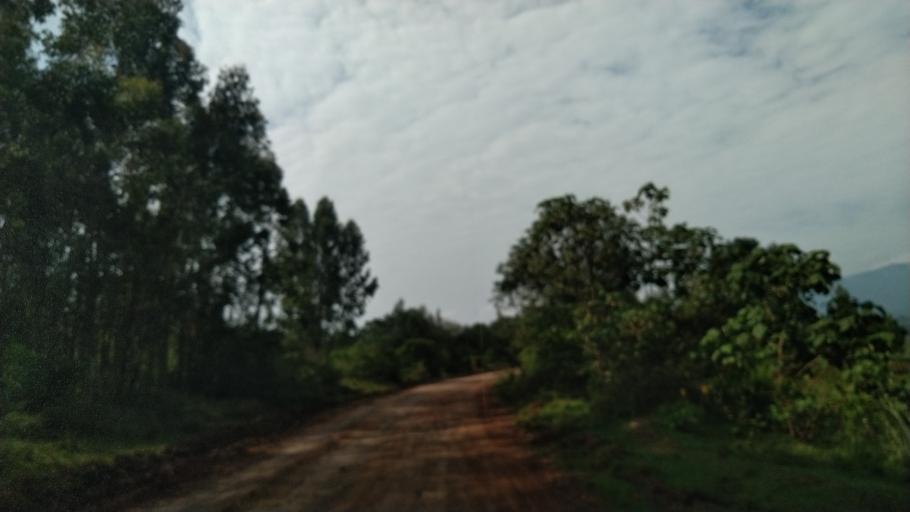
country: ET
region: Oromiya
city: Jima
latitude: 7.6681
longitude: 37.2443
